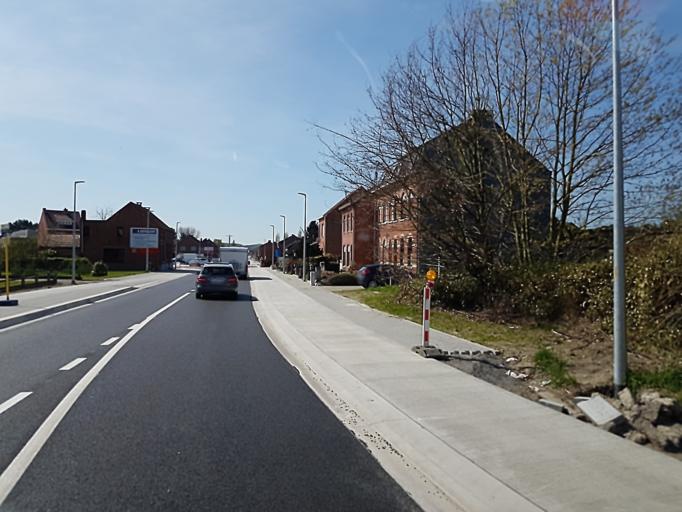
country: BE
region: Flanders
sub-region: Provincie Vlaams-Brabant
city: Aarschot
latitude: 51.0051
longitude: 4.8368
